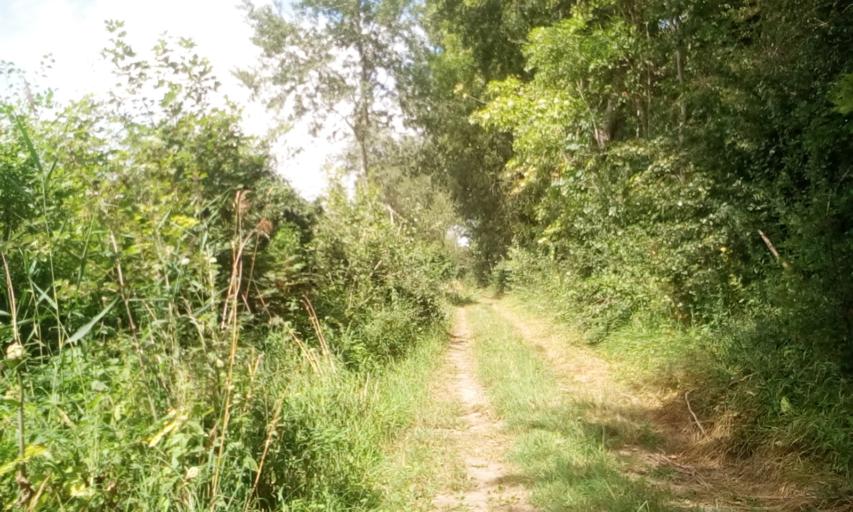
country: FR
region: Lower Normandy
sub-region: Departement du Calvados
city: Bellengreville
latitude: 49.1545
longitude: -0.2059
